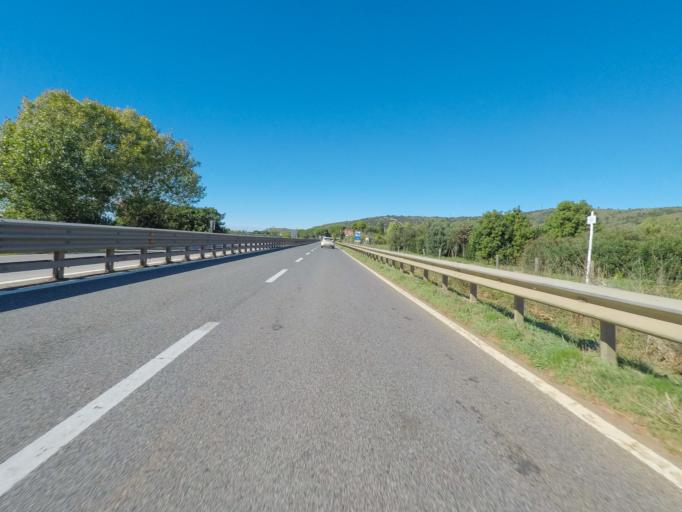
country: IT
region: Tuscany
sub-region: Provincia di Grosseto
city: Orbetello Scalo
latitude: 42.4339
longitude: 11.2819
